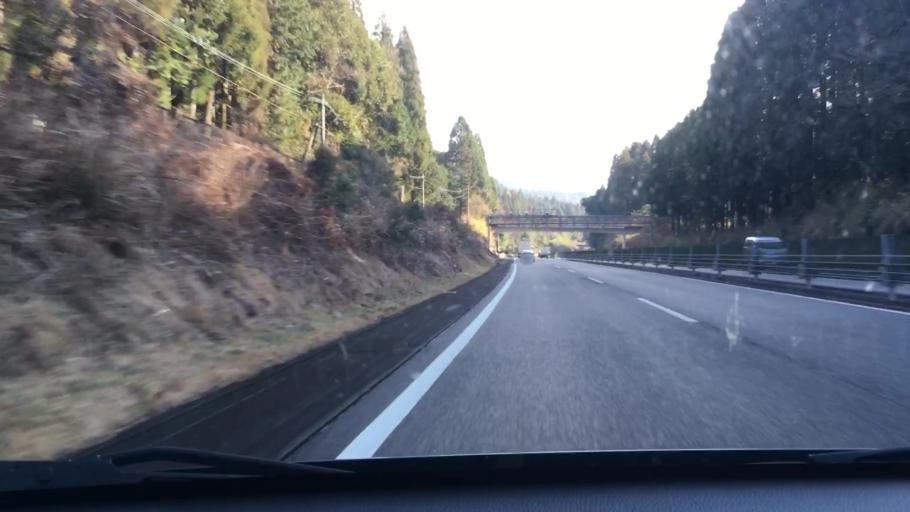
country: JP
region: Kagoshima
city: Okuchi-shinohara
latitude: 32.0027
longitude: 130.7567
